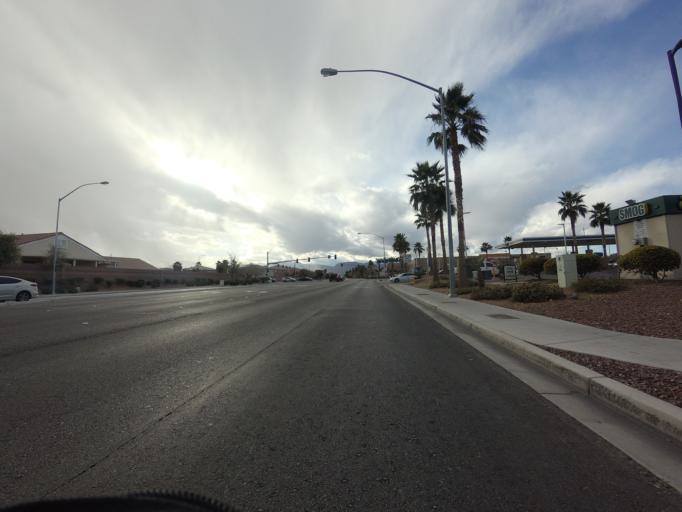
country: US
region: Nevada
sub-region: Clark County
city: North Las Vegas
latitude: 36.2691
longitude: -115.2057
